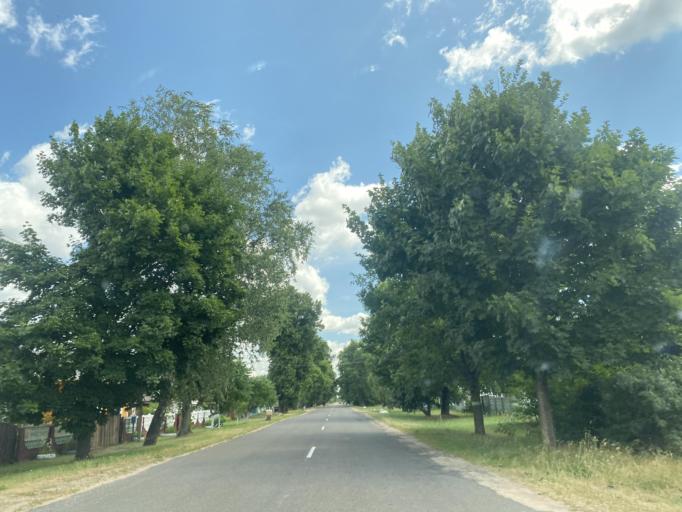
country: BY
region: Brest
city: Ivanava
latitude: 52.1680
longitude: 25.5546
